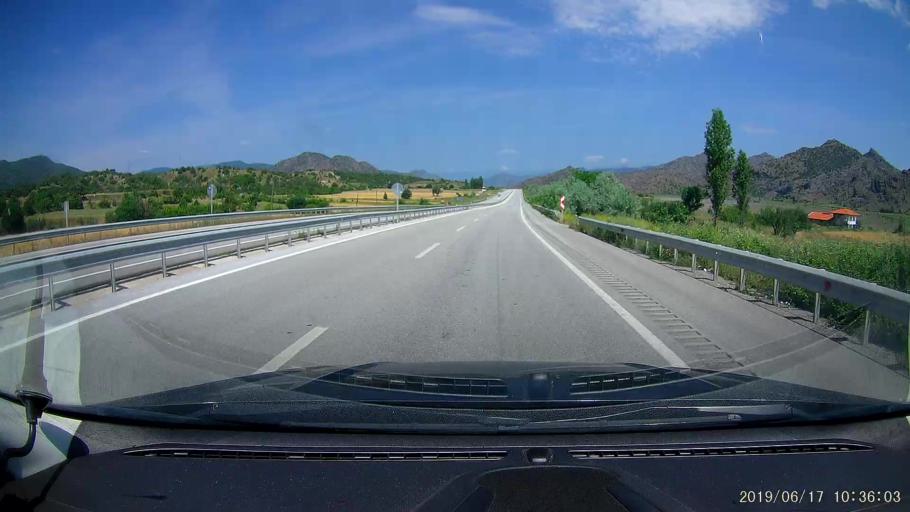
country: TR
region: Corum
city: Osmancik
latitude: 40.9735
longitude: 34.6888
